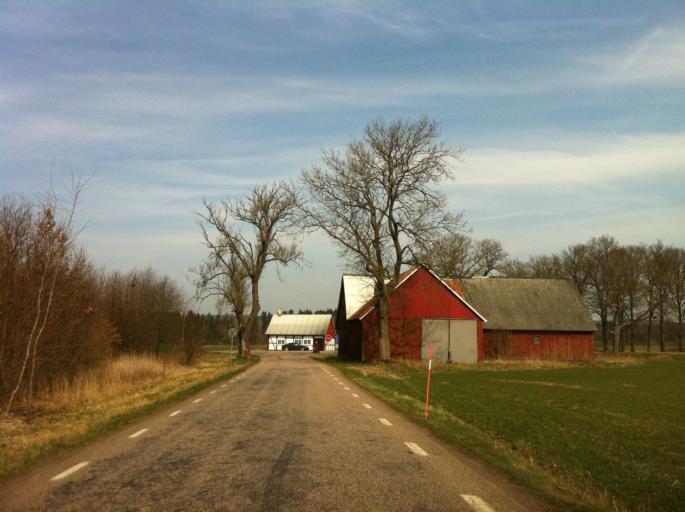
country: SE
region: Skane
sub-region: Svalovs Kommun
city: Kagerod
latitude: 55.9790
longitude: 13.1224
